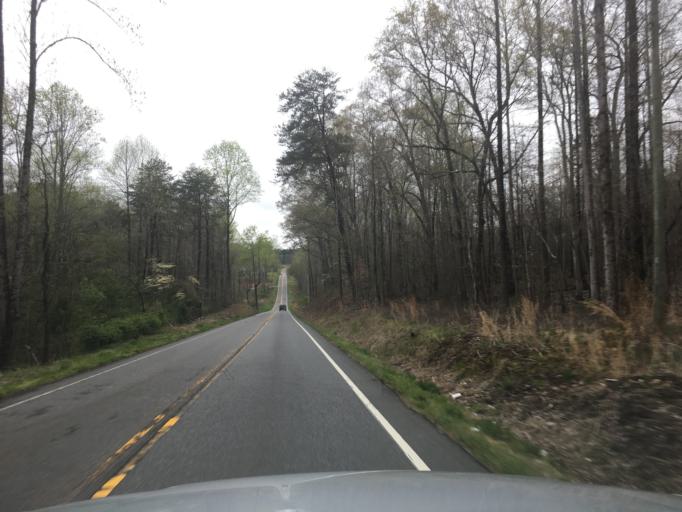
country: US
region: South Carolina
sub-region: Spartanburg County
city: Fairforest
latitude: 34.9700
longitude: -82.0406
